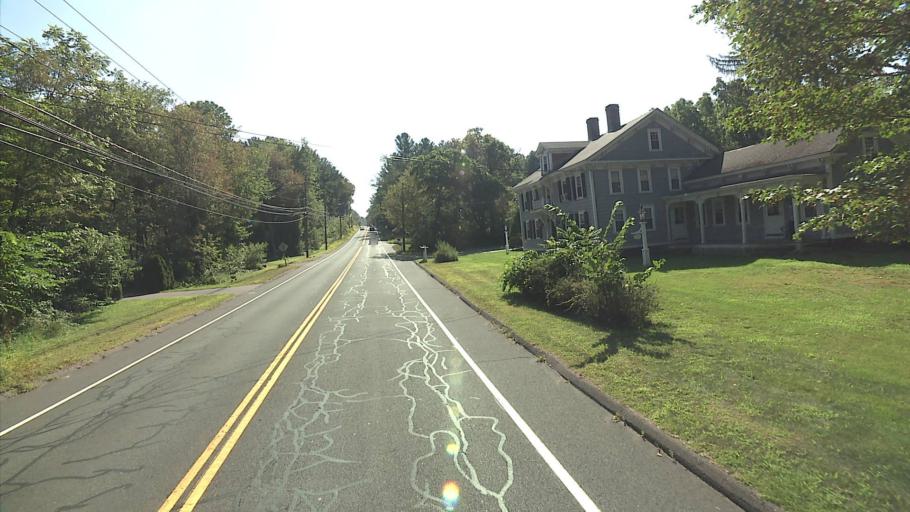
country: US
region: Connecticut
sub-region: Tolland County
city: Somers
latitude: 41.9845
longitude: -72.4326
